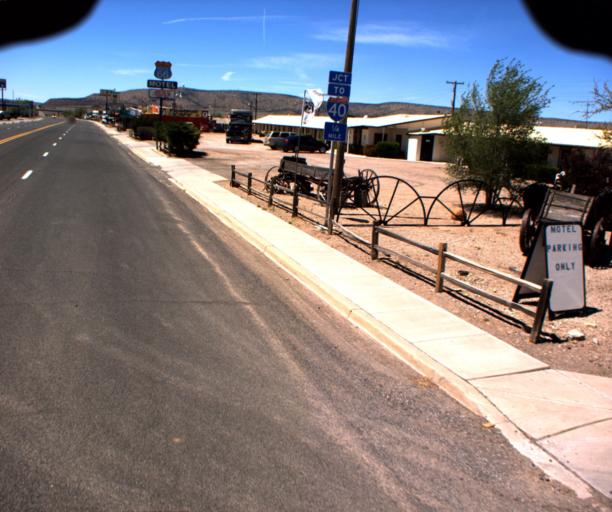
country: US
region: Arizona
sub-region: Mohave County
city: Peach Springs
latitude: 35.3281
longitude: -112.8818
